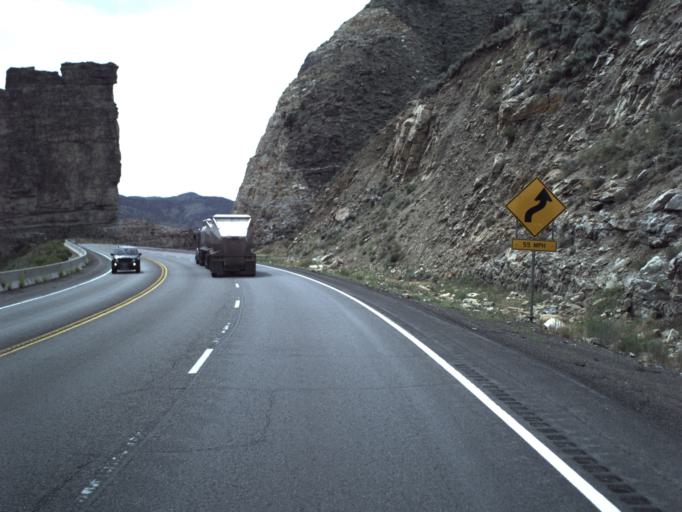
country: US
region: Utah
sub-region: Carbon County
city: Helper
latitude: 39.7529
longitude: -110.8875
